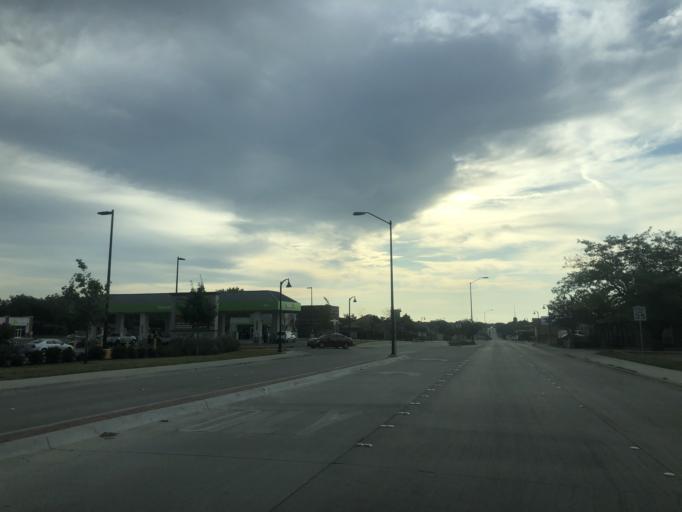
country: US
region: Texas
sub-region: Tarrant County
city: Hurst
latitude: 32.8236
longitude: -97.1850
